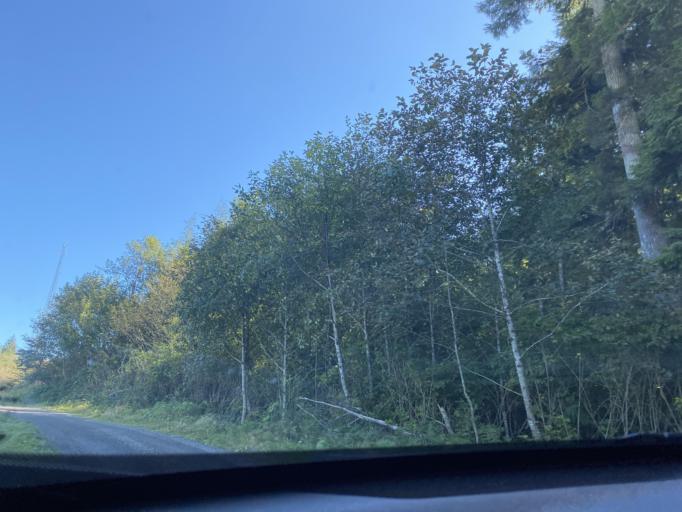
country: US
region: Washington
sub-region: Clallam County
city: Forks
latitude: 47.8978
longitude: -124.6206
